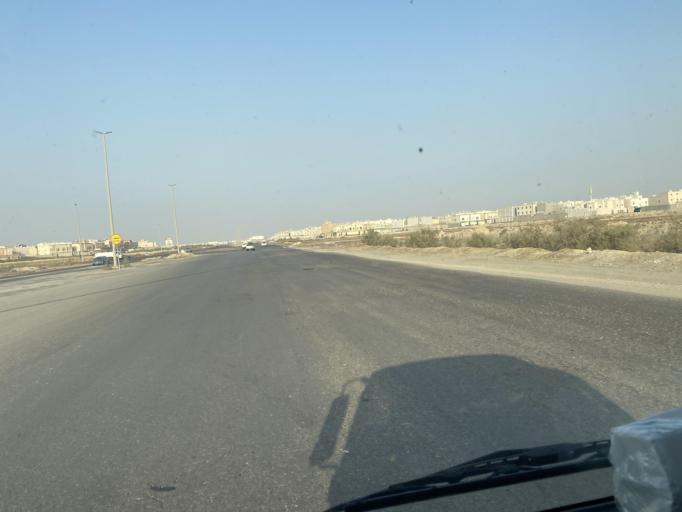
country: SA
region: Eastern Province
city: Sayhat
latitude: 26.4022
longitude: 49.9943
